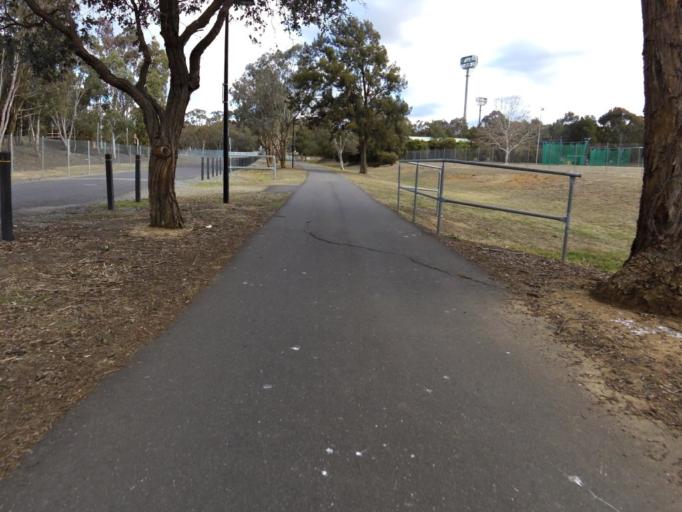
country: AU
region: Australian Capital Territory
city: Kaleen
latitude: -35.2476
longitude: 149.1054
